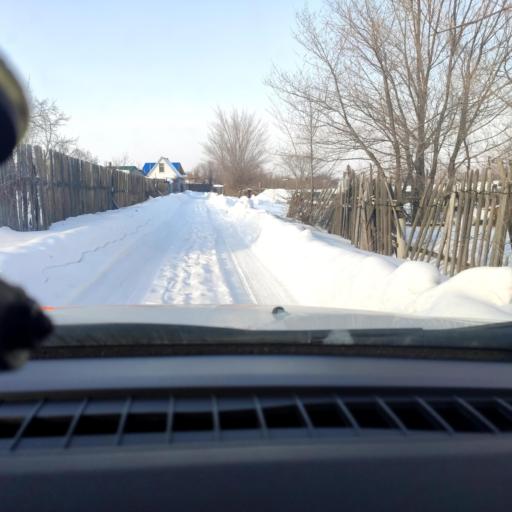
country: RU
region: Samara
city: Samara
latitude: 53.1304
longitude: 50.2593
